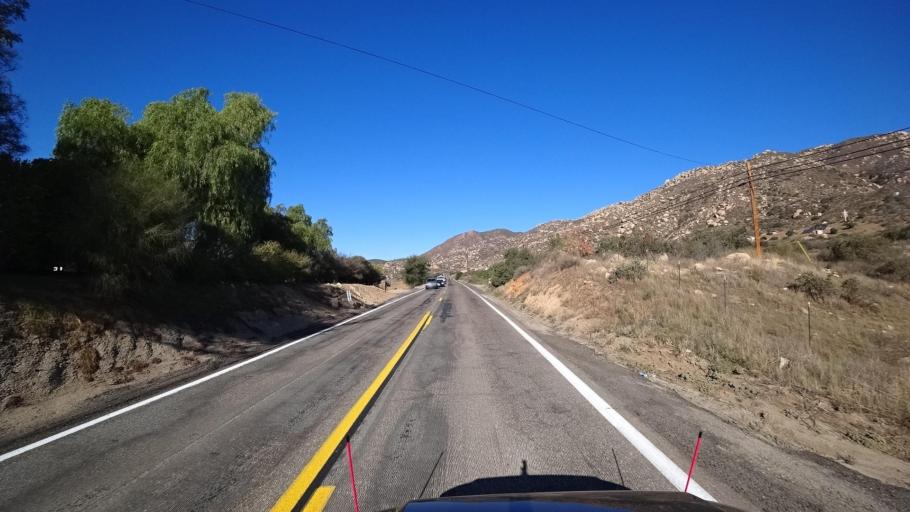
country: MX
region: Baja California
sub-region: Tecate
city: Lomas de Santa Anita
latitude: 32.6127
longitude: -116.7095
